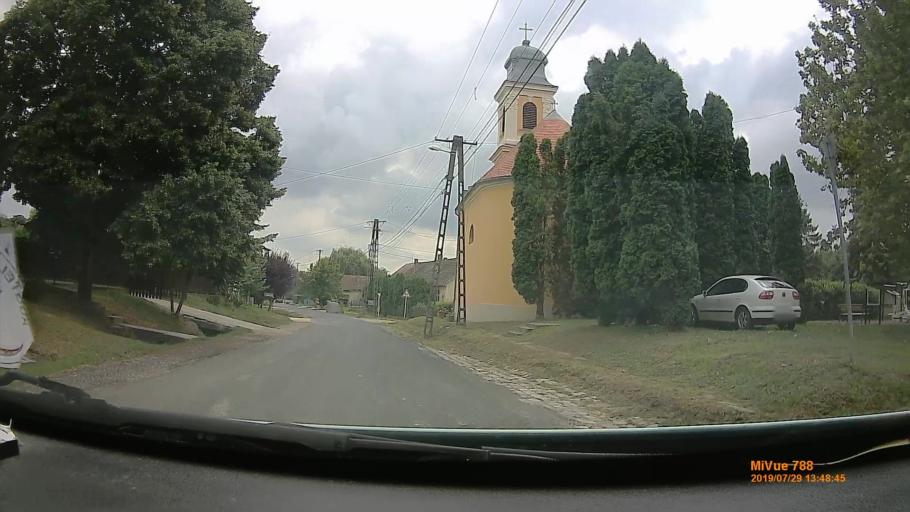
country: HU
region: Somogy
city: Tab
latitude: 46.7829
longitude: 17.9515
